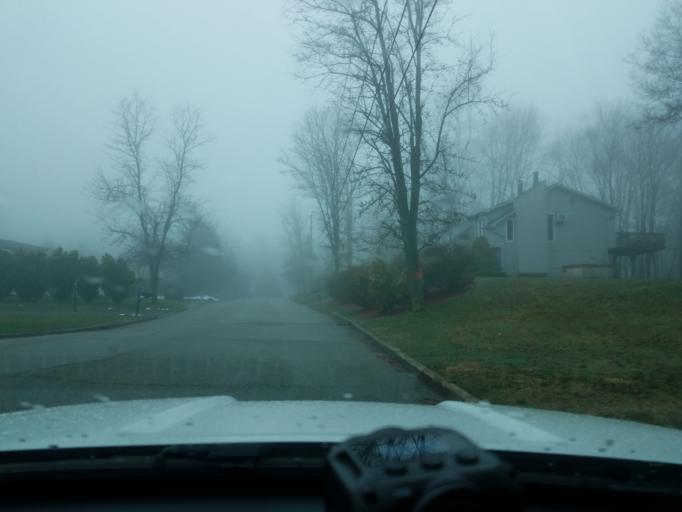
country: US
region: Connecticut
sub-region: New Haven County
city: Naugatuck
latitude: 41.5005
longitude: -73.0170
